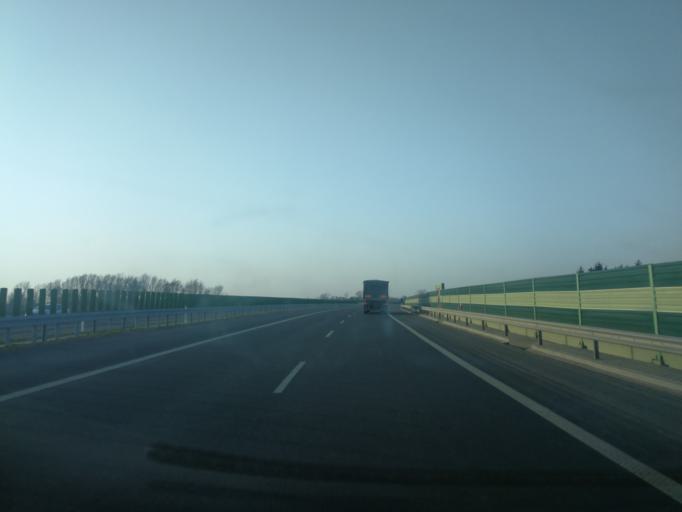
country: PL
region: Pomeranian Voivodeship
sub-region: Powiat nowodworski
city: Nowy Dwor Gdanski
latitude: 54.2008
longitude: 19.1154
